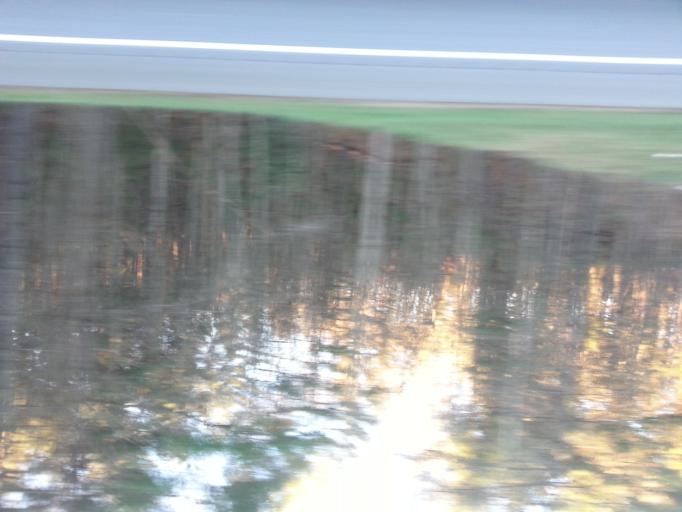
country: US
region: North Carolina
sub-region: Buncombe County
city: Bent Creek
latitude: 35.5034
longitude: -82.5698
